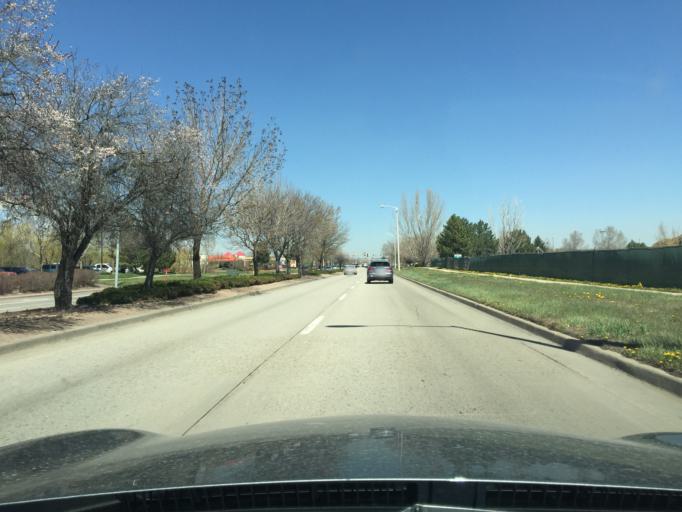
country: US
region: Colorado
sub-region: Boulder County
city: Longmont
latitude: 40.1477
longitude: -105.1307
